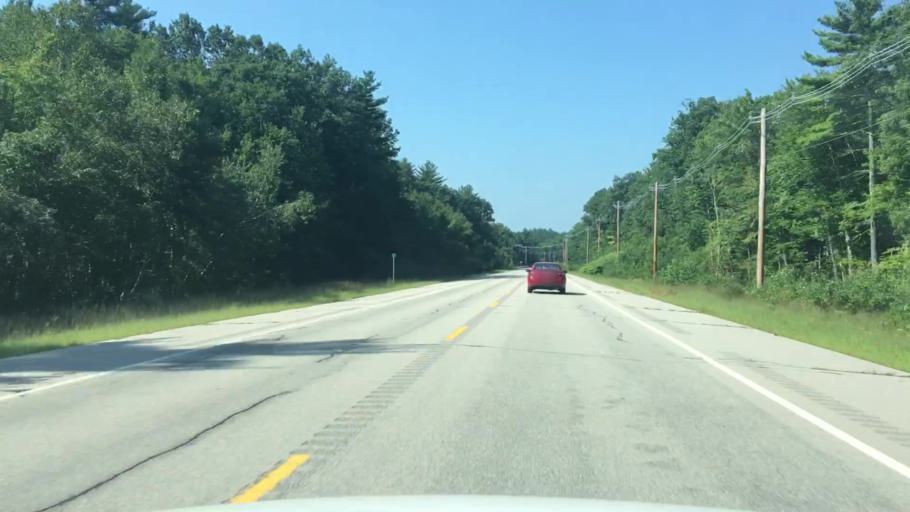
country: US
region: New Hampshire
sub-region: Rockingham County
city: Danville
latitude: 42.9019
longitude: -71.1103
